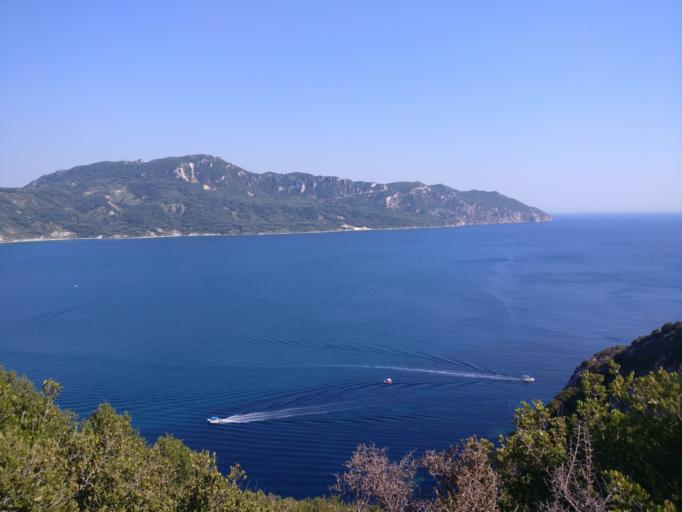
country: GR
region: Ionian Islands
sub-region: Nomos Kerkyras
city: Agios Georgis
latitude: 39.7179
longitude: 19.6587
